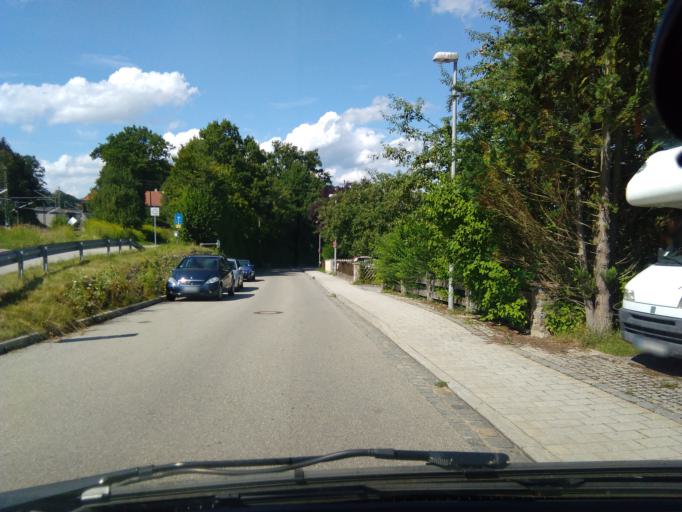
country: DE
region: Bavaria
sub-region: Upper Bavaria
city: Assling
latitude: 47.9920
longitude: 11.9930
